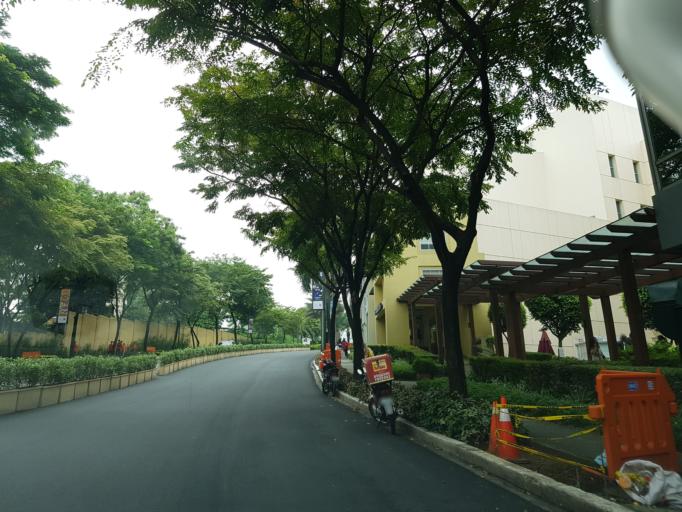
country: PH
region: Metro Manila
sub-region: Makati City
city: Makati City
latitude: 14.5350
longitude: 121.0480
